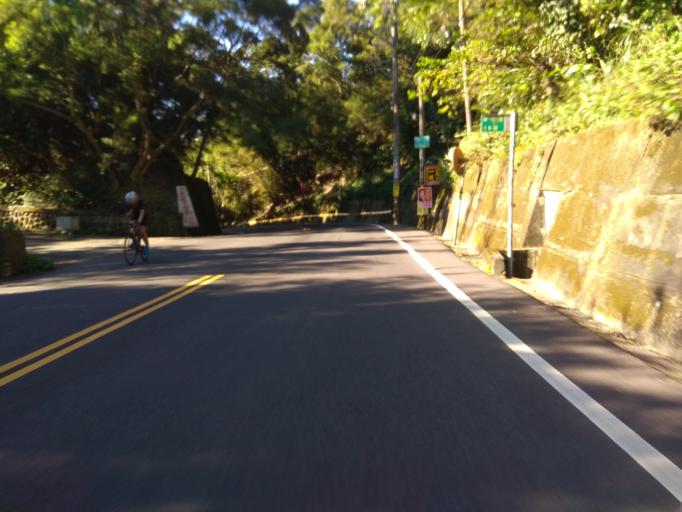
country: TW
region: Taiwan
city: Daxi
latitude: 24.8611
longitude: 121.1544
